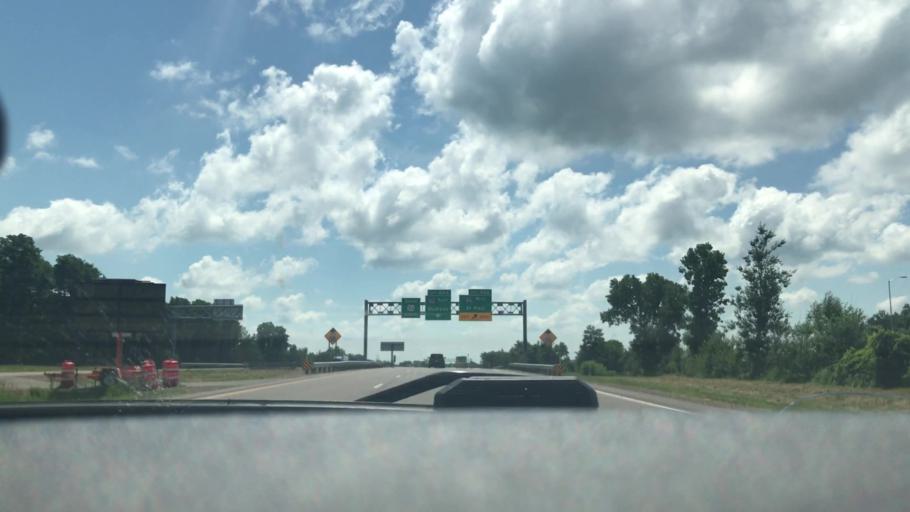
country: US
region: Wisconsin
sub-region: Eau Claire County
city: Altoona
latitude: 44.7739
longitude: -91.4304
